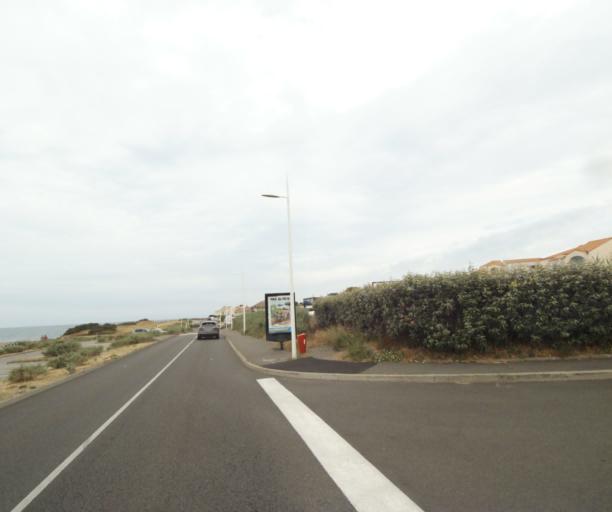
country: FR
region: Pays de la Loire
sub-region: Departement de la Vendee
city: Chateau-d'Olonne
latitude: 46.4745
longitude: -1.7521
